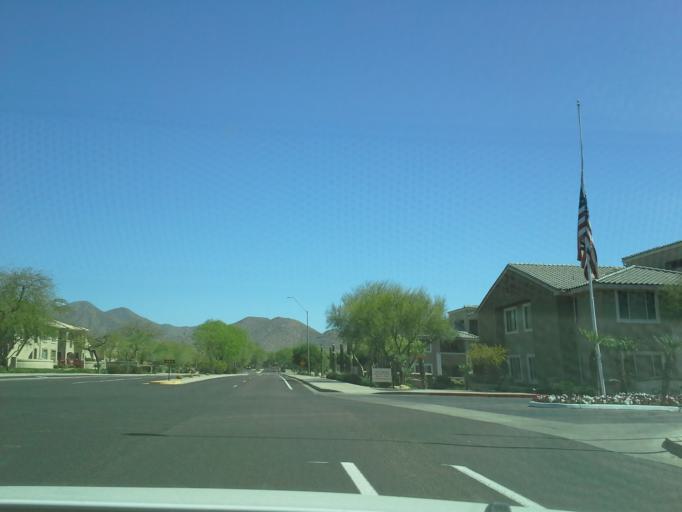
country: US
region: Arizona
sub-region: Maricopa County
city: Paradise Valley
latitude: 33.6115
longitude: -111.8766
